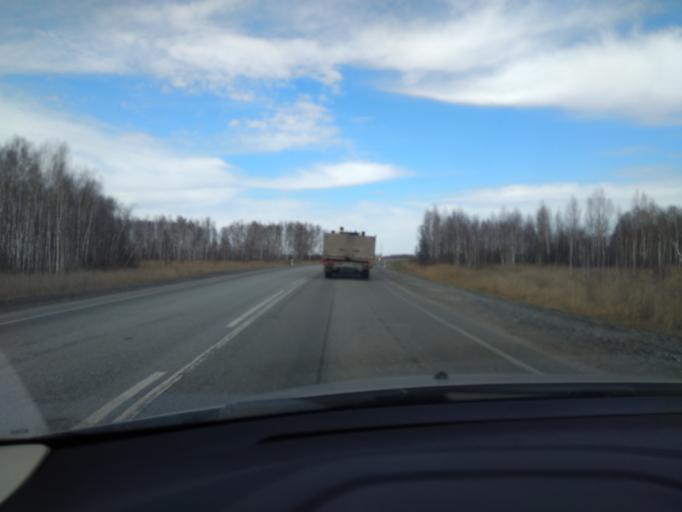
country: RU
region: Sverdlovsk
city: Pyshma
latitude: 56.9760
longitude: 63.2348
